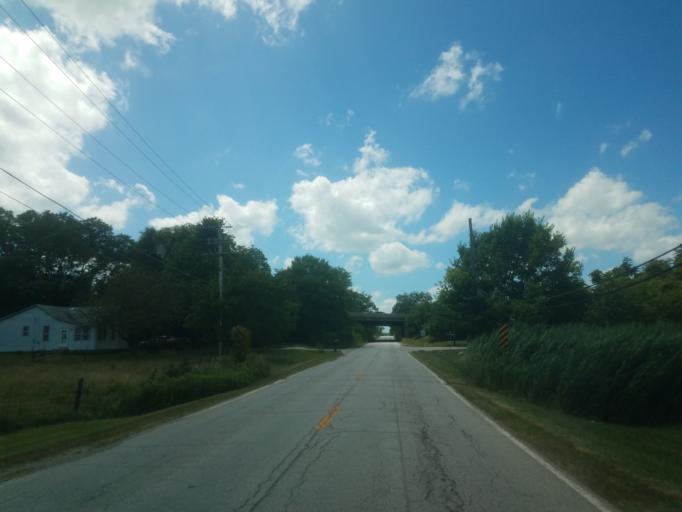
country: US
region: Illinois
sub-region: McLean County
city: Bloomington
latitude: 40.4588
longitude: -89.0256
